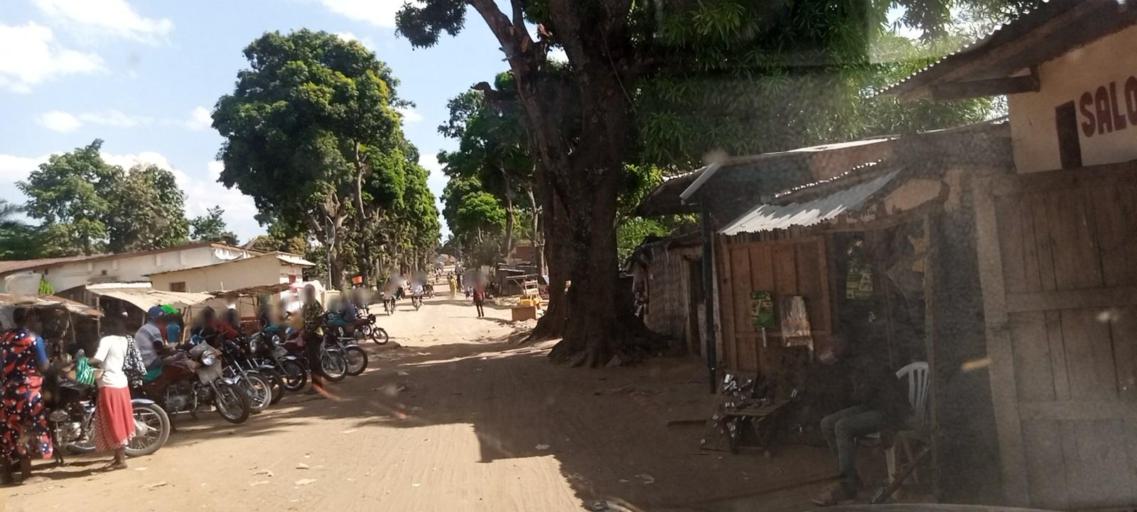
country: CD
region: Kasai-Oriental
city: Kabinda
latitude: -6.1316
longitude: 24.4891
